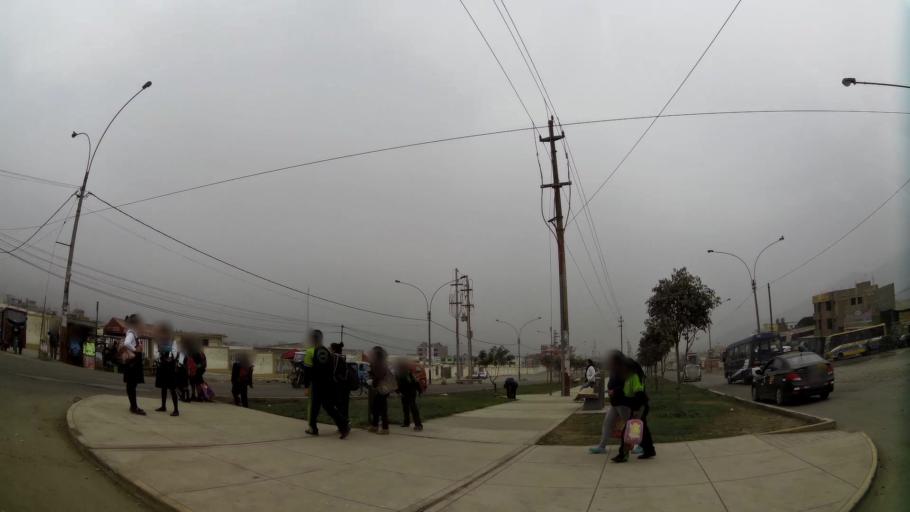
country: PE
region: Lima
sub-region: Lima
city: Urb. Santo Domingo
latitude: -11.9223
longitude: -76.9609
